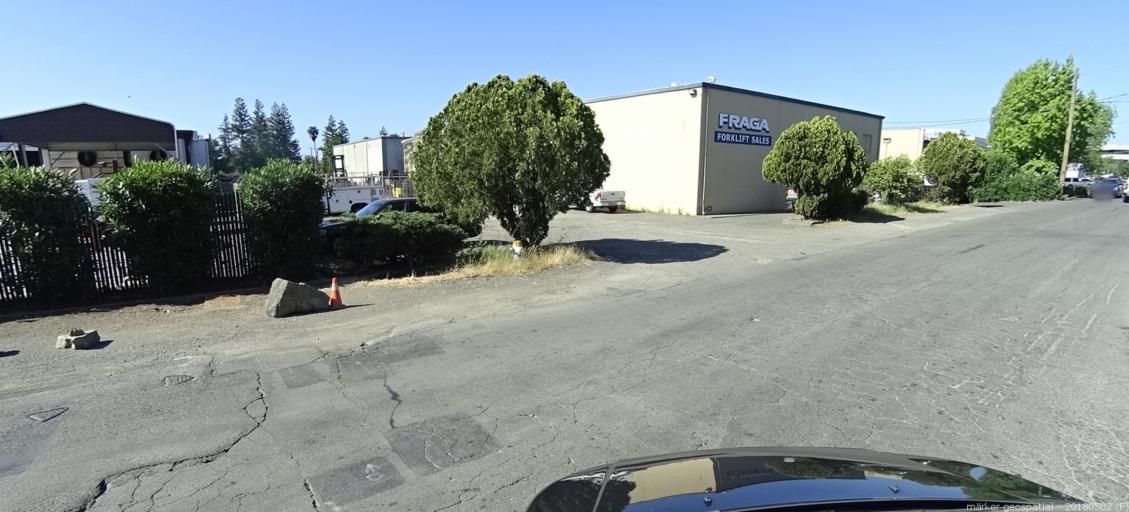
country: US
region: California
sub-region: Sacramento County
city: Arden-Arcade
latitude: 38.6087
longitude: -121.4316
